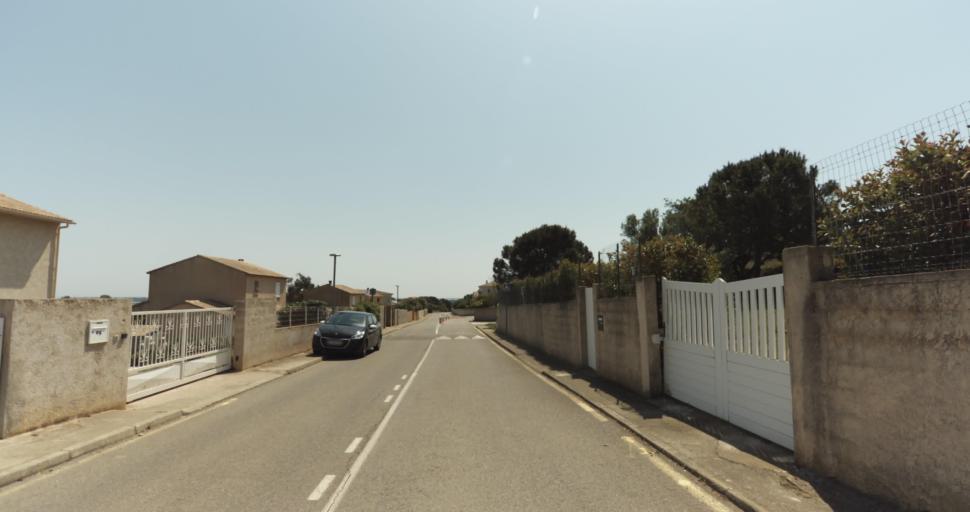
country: FR
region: Corsica
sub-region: Departement de la Haute-Corse
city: Biguglia
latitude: 42.6068
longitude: 9.4302
